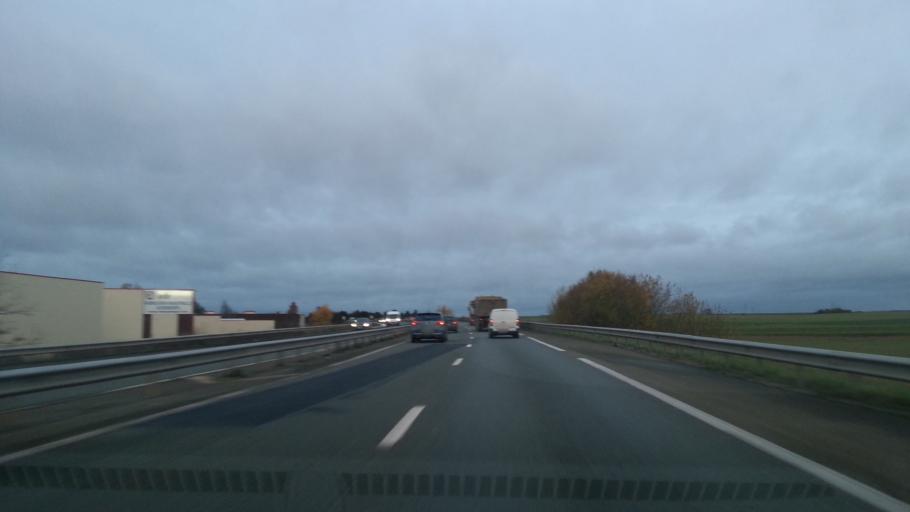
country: FR
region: Picardie
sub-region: Departement de l'Oise
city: Bresles
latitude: 49.4171
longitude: 2.2578
